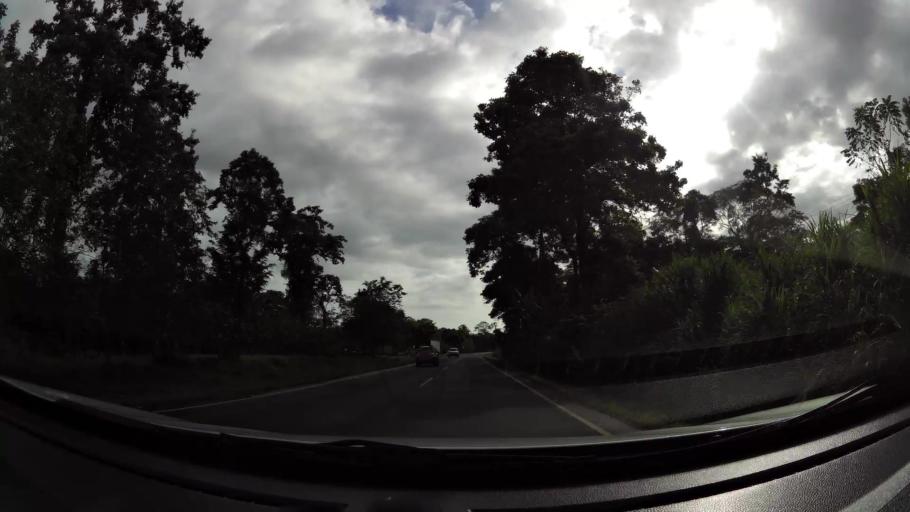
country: CR
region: Limon
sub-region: Canton de Guacimo
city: Guacimo
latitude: 10.2056
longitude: -83.7347
